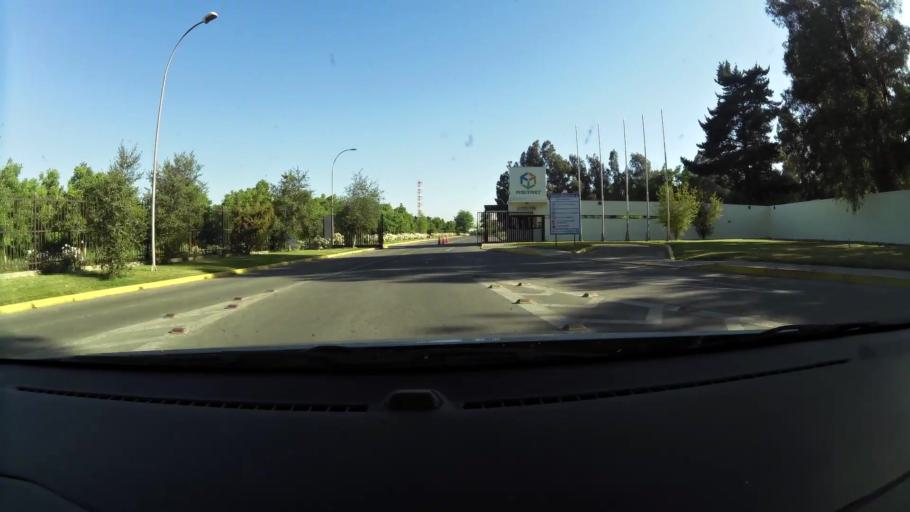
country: CL
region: Santiago Metropolitan
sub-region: Provincia de Maipo
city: San Bernardo
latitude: -33.6399
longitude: -70.7000
